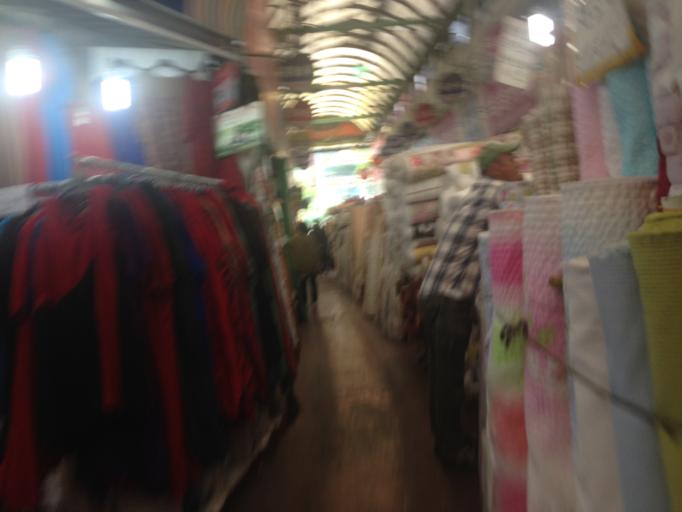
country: KR
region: Seoul
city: Seoul
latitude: 37.5699
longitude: 127.0004
